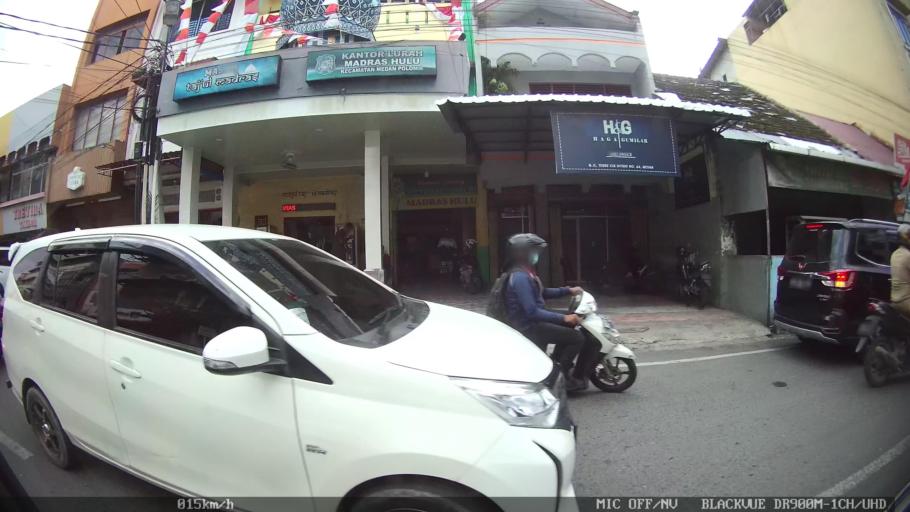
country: ID
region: North Sumatra
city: Medan
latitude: 3.5826
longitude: 98.6688
